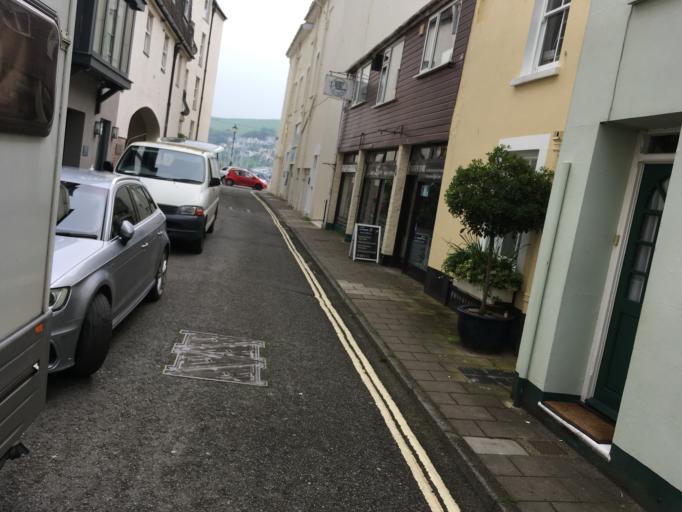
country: GB
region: England
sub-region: Devon
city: Dartmouth
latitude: 50.3497
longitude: -3.5781
